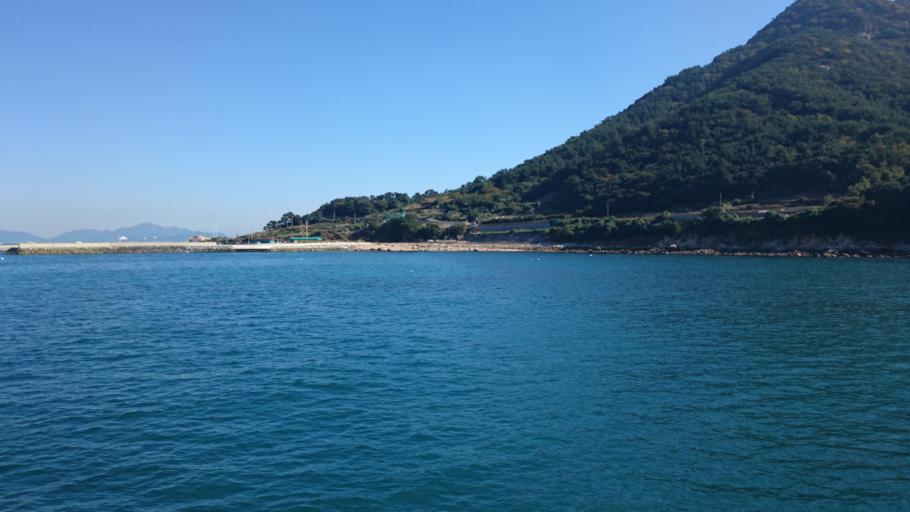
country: KR
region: Gyeongsangnam-do
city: Kyosai
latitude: 34.7174
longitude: 128.4545
